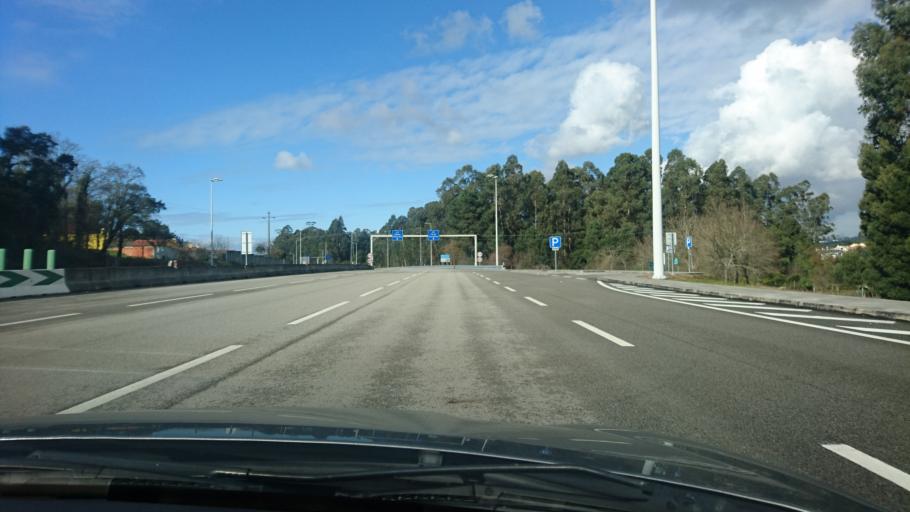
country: PT
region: Aveiro
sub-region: Santa Maria da Feira
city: Feira
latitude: 40.9281
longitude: -8.5656
